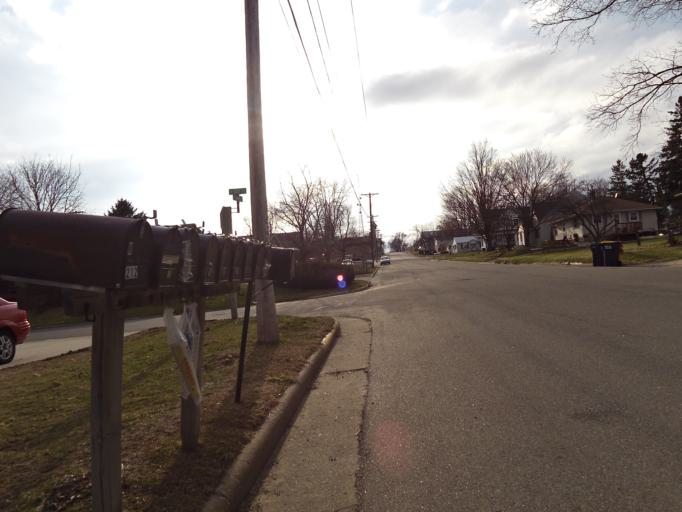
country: US
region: Wisconsin
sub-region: Pierce County
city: Ellsworth
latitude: 44.7330
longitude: -92.4804
